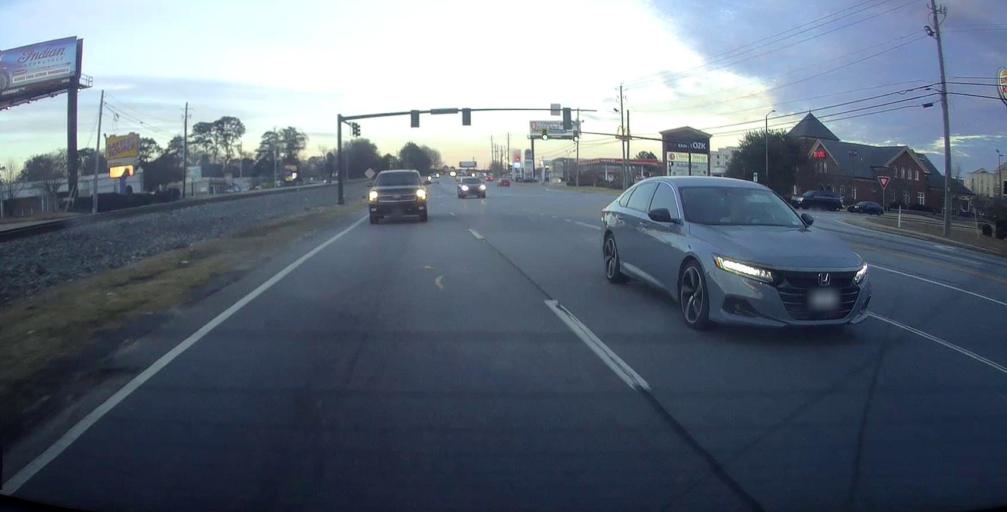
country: US
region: Alabama
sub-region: Russell County
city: Phenix City
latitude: 32.5525
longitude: -84.9487
